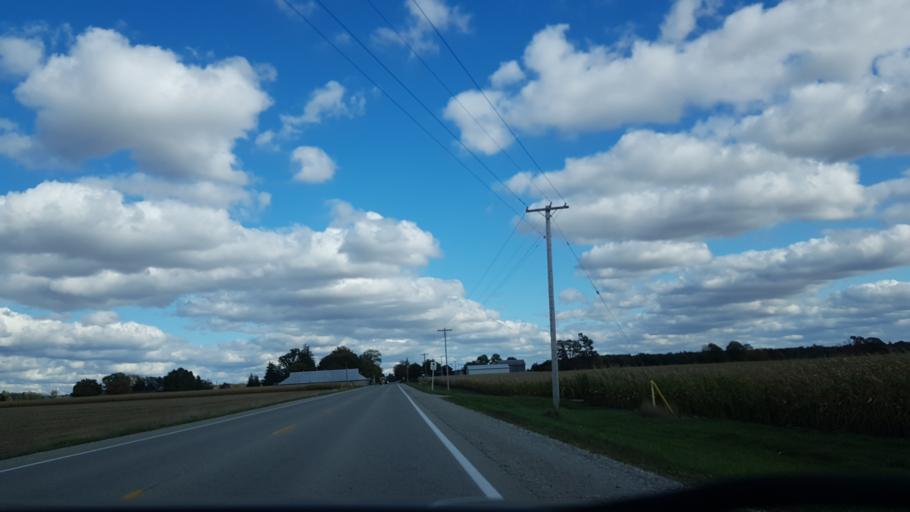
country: CA
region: Ontario
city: South Huron
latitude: 43.2422
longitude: -81.7227
